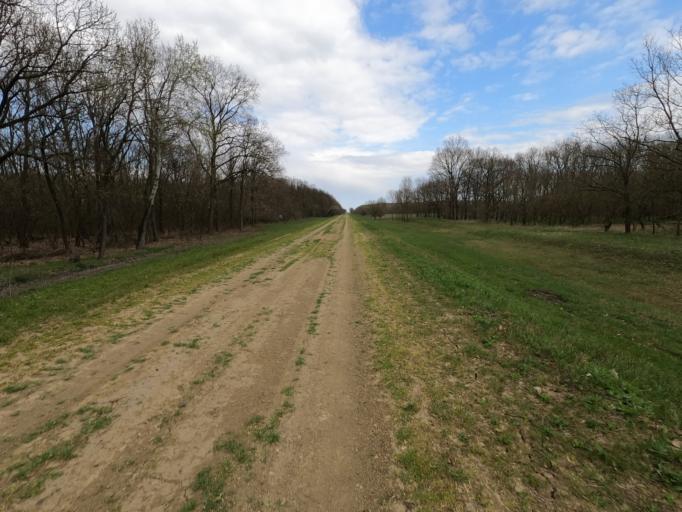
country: HU
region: Jasz-Nagykun-Szolnok
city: Turkeve
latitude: 47.0978
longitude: 20.7892
